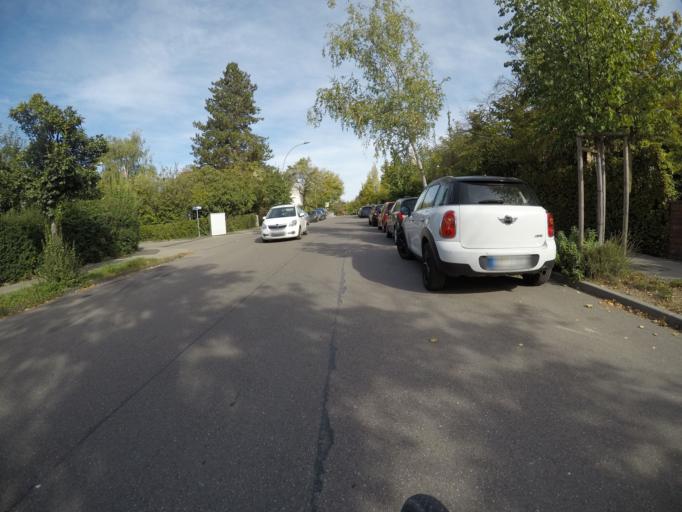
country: DE
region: Baden-Wuerttemberg
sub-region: Regierungsbezirk Stuttgart
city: Korntal
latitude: 48.8292
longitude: 9.1169
